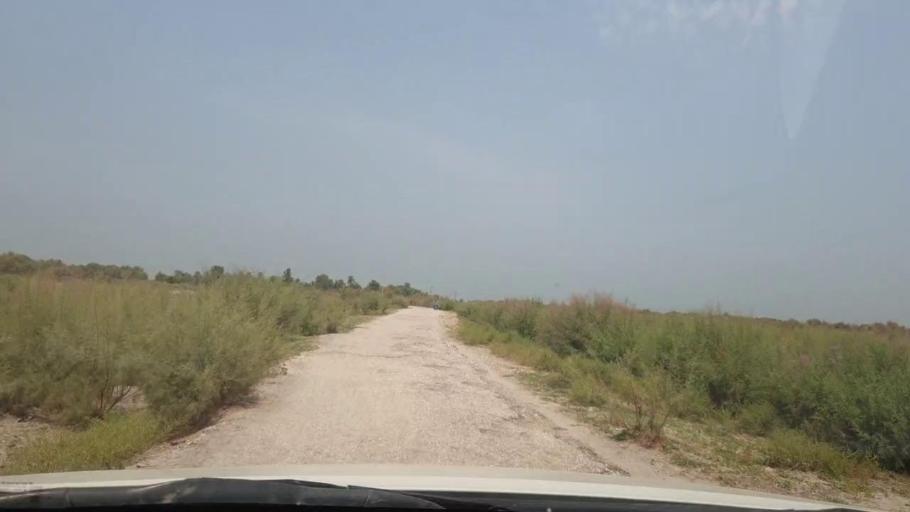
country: PK
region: Sindh
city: Rustam jo Goth
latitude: 28.0557
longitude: 68.7524
